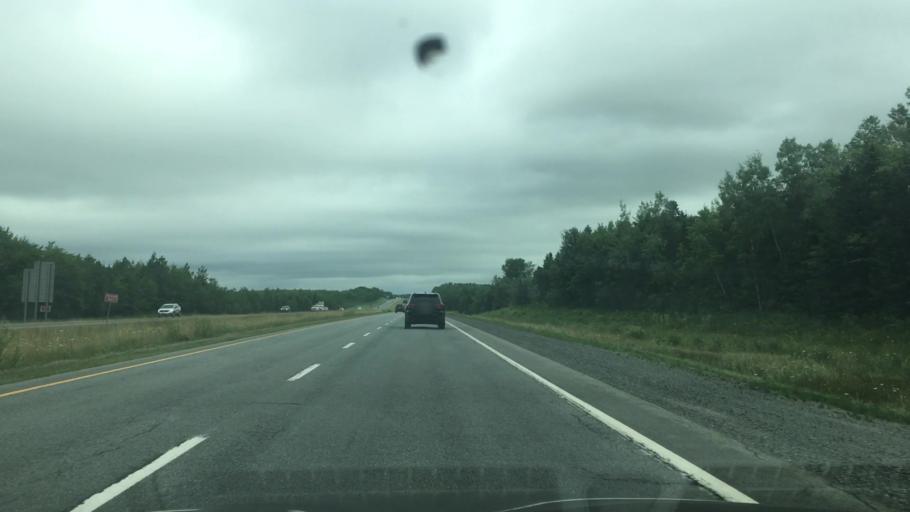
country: CA
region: Nova Scotia
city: Cole Harbour
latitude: 44.9938
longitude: -63.4935
